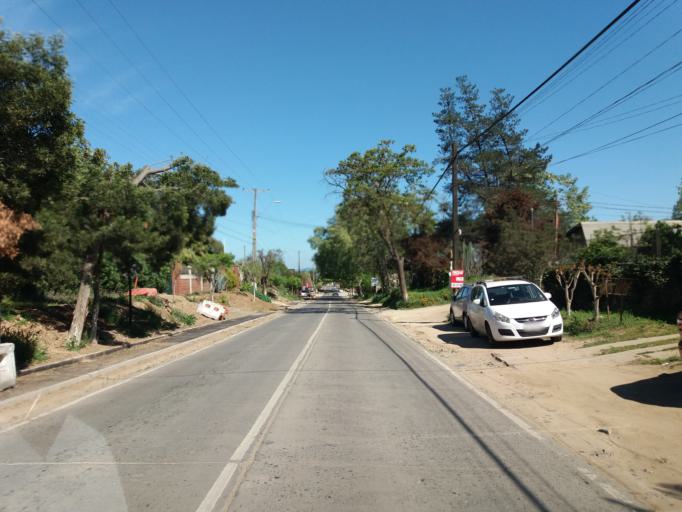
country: CL
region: Valparaiso
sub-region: Provincia de Marga Marga
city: Limache
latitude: -33.0006
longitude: -71.2035
